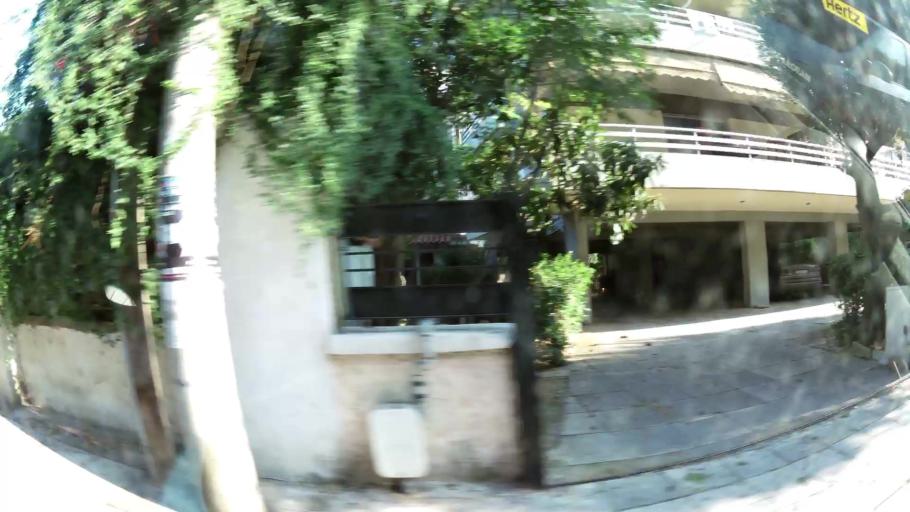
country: GR
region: Attica
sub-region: Nomarchia Athinas
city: Agia Paraskevi
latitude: 38.0102
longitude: 23.8274
